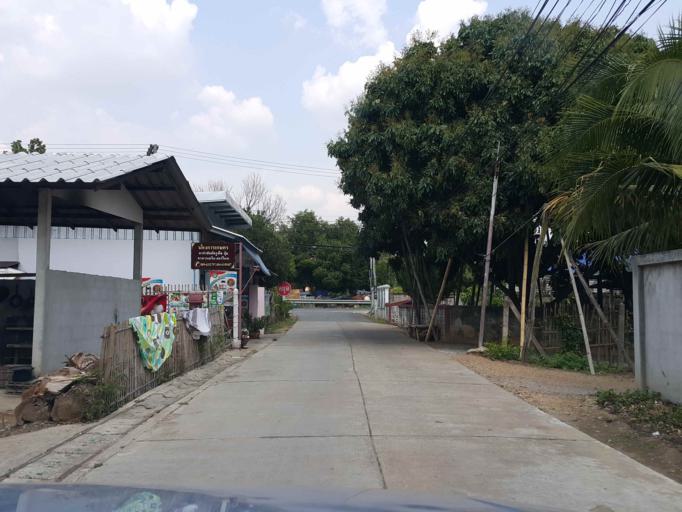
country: TH
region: Chiang Mai
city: Saraphi
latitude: 18.6992
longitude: 98.9852
